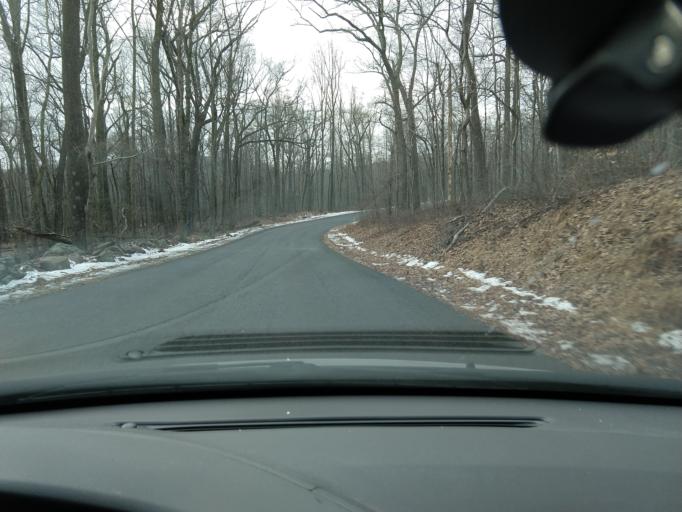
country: US
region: Pennsylvania
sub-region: Berks County
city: Birdsboro
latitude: 40.2105
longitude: -75.7739
